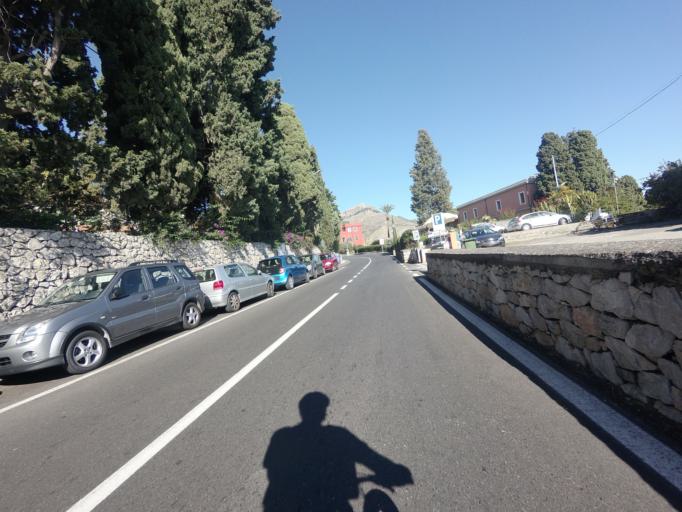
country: IT
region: Sicily
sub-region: Messina
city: Taormina
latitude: 37.8520
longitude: 15.2952
